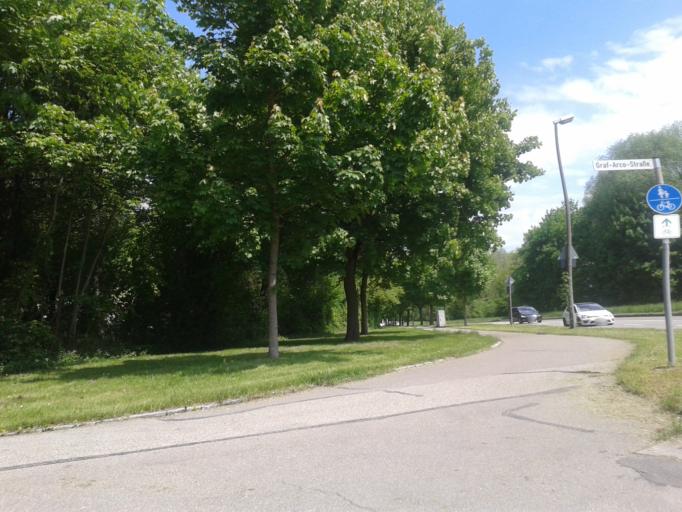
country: DE
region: Baden-Wuerttemberg
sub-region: Tuebingen Region
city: Ulm
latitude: 48.3553
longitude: 9.9463
